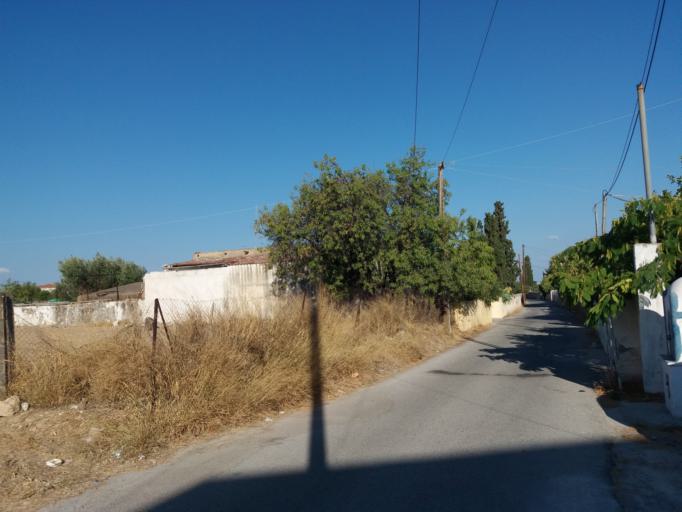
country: GR
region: Attica
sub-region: Nomos Piraios
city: Aegina
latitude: 37.7551
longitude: 23.4376
